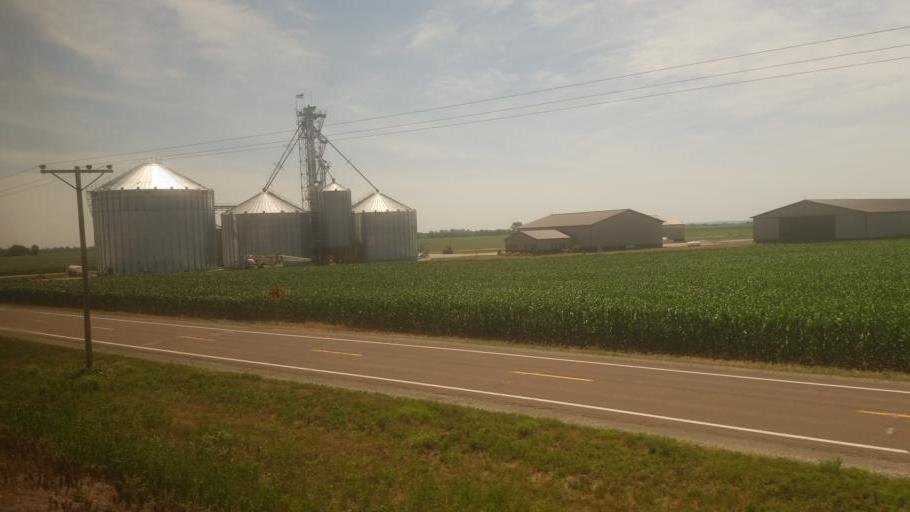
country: US
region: Missouri
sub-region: Carroll County
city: Carrollton
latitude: 39.3172
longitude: -93.6128
